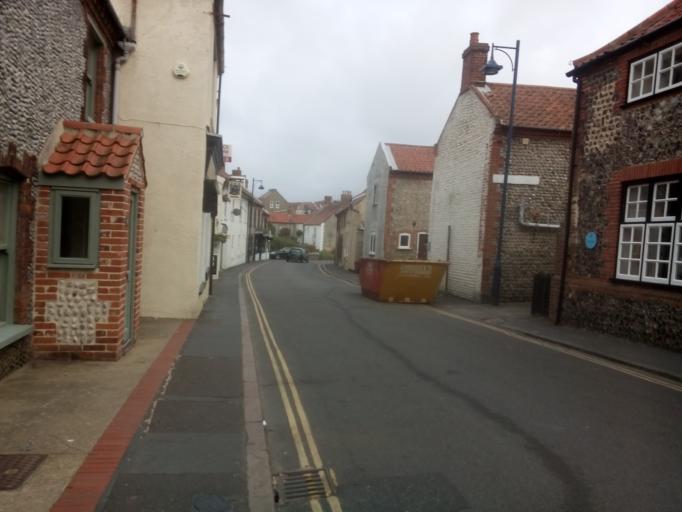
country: GB
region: England
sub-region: Norfolk
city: Sheringham
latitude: 52.9446
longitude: 1.2128
